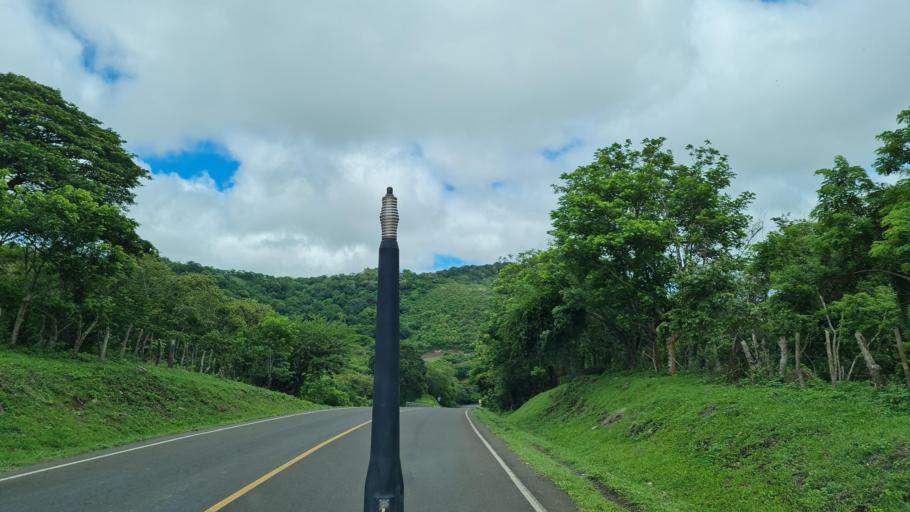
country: NI
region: Matagalpa
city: Terrabona
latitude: 12.5915
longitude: -85.9367
